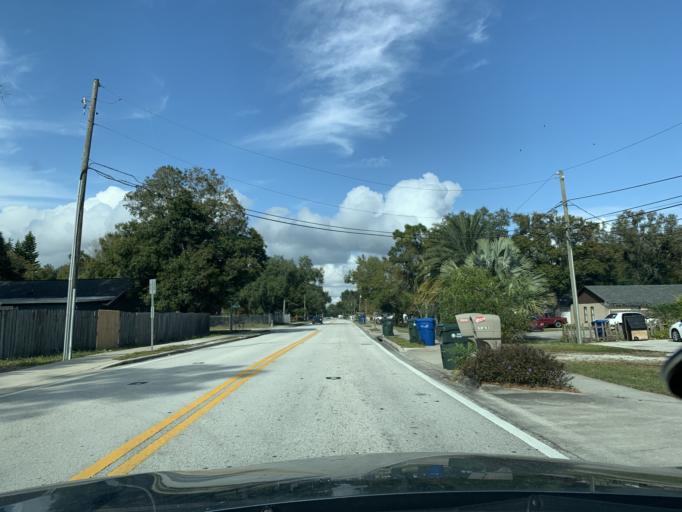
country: US
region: Florida
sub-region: Pinellas County
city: South Highpoint
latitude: 27.9113
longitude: -82.7131
